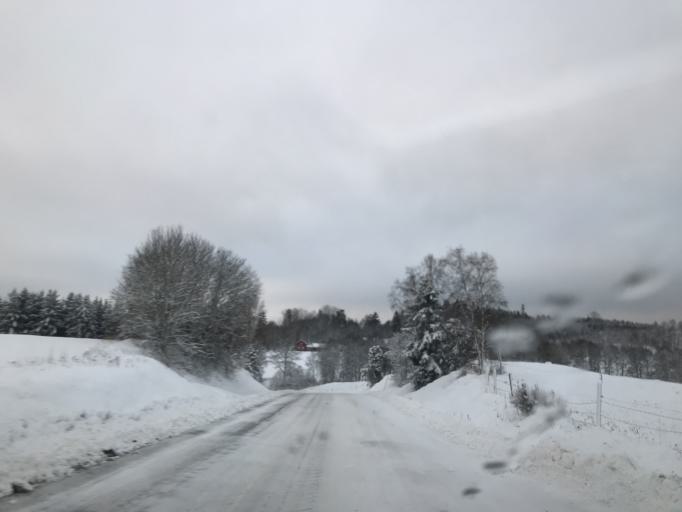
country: SE
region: Vaestra Goetaland
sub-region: Svenljunga Kommun
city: Svenljunga
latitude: 57.3917
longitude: 13.0660
